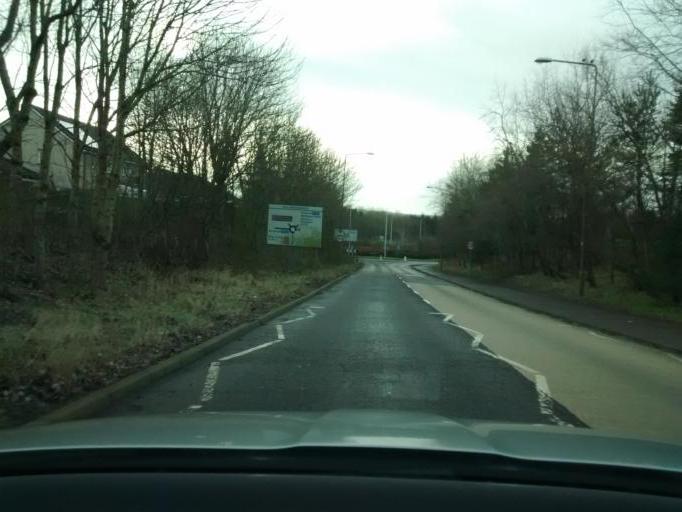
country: GB
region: Scotland
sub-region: West Lothian
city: Livingston
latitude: 55.8891
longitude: -3.5504
